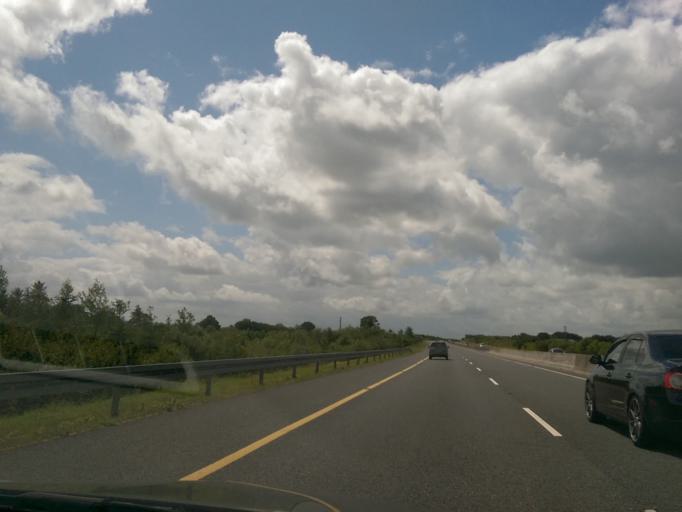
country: IE
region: Munster
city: Cahir
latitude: 52.3385
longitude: -8.0240
